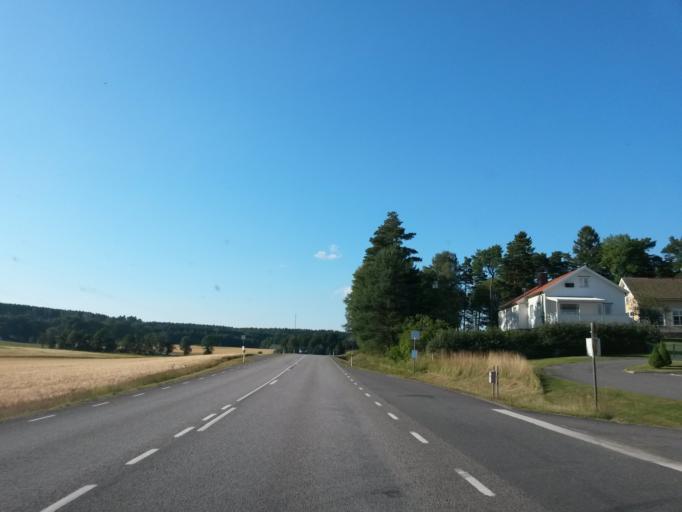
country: SE
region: Vaestra Goetaland
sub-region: Vargarda Kommun
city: Jonstorp
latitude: 58.0087
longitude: 12.6269
